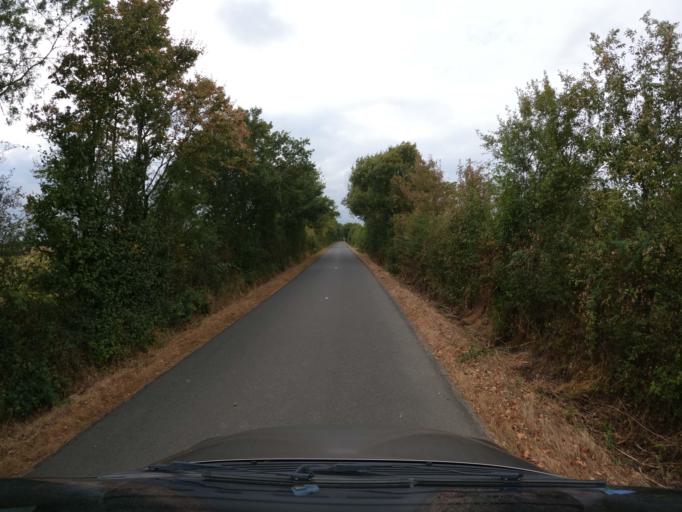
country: FR
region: Pays de la Loire
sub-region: Departement de Maine-et-Loire
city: Saint-Christophe-du-Bois
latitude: 47.0436
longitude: -0.9807
